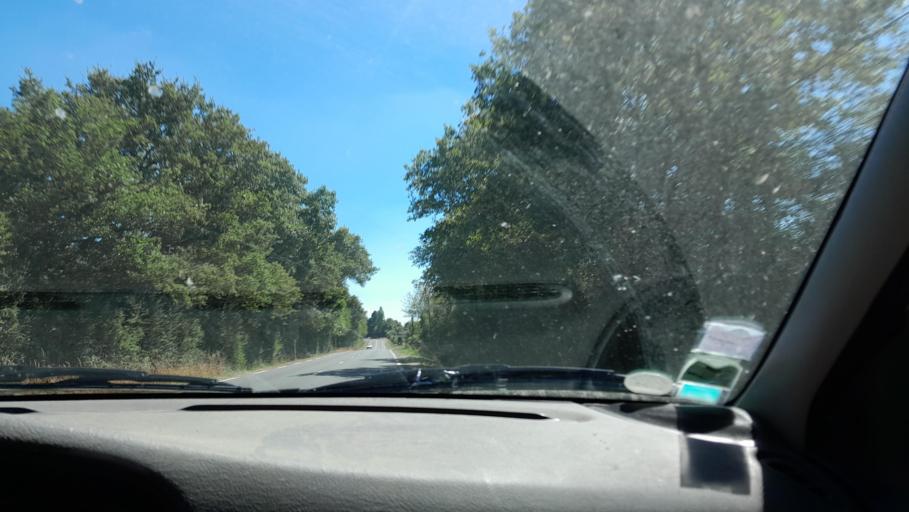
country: FR
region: Pays de la Loire
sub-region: Departement de la Loire-Atlantique
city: Saint-Mars-la-Jaille
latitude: 47.6064
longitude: -1.2018
